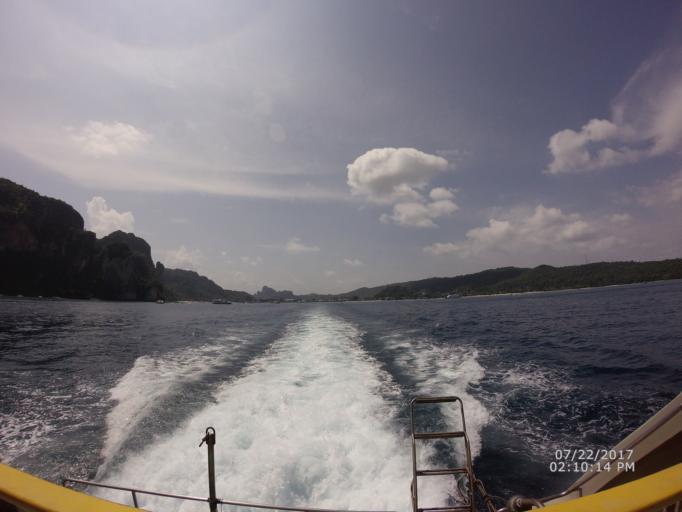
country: TH
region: Krabi
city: Saladan
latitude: 7.7250
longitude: 98.7724
